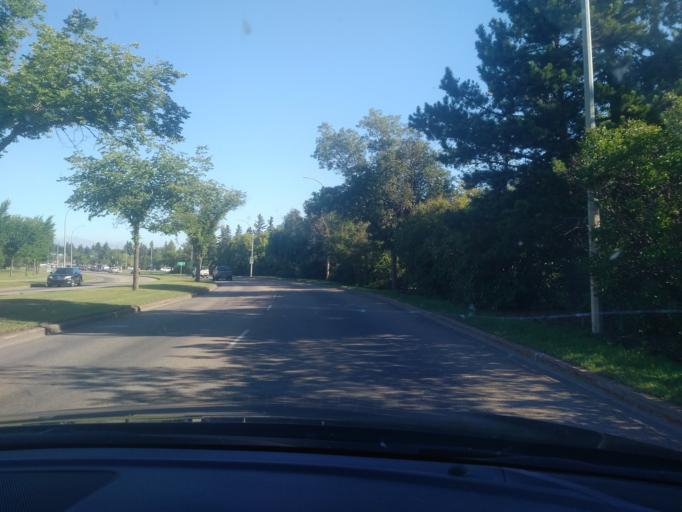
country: CA
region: Alberta
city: Edmonton
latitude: 53.5056
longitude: -113.5227
